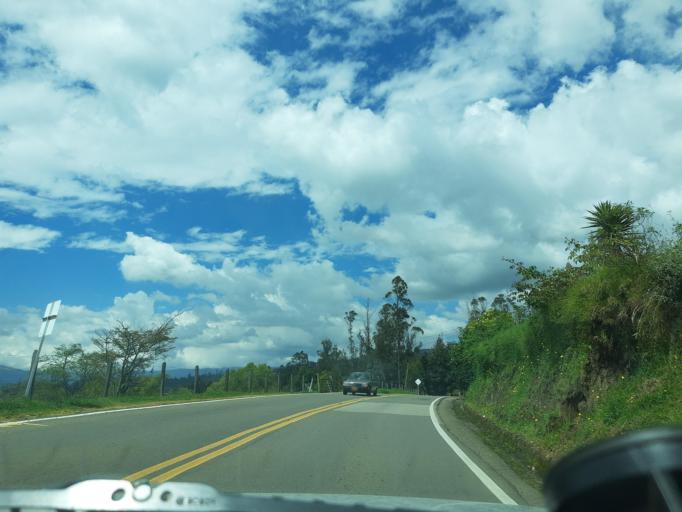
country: CO
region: Boyaca
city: Sutamarchan
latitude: 5.5977
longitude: -73.7165
